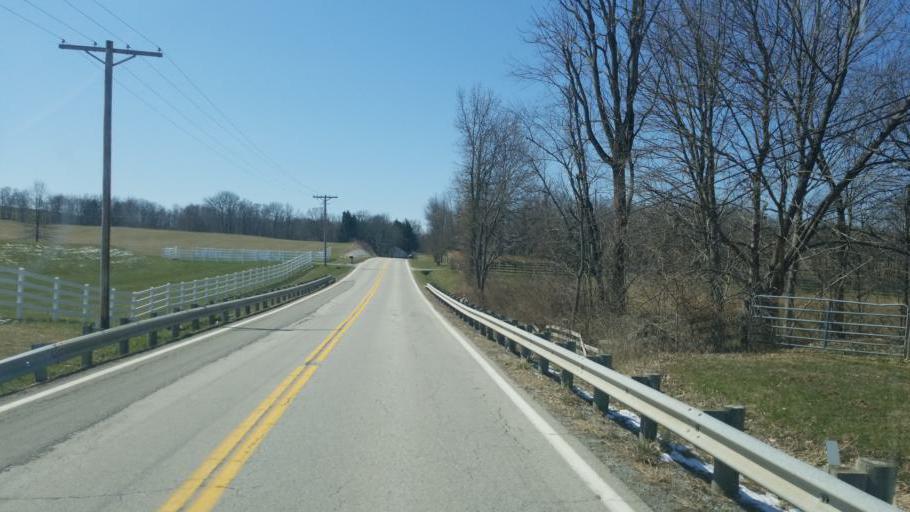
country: US
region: Ohio
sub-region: Highland County
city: Hillsboro
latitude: 39.2241
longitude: -83.5833
